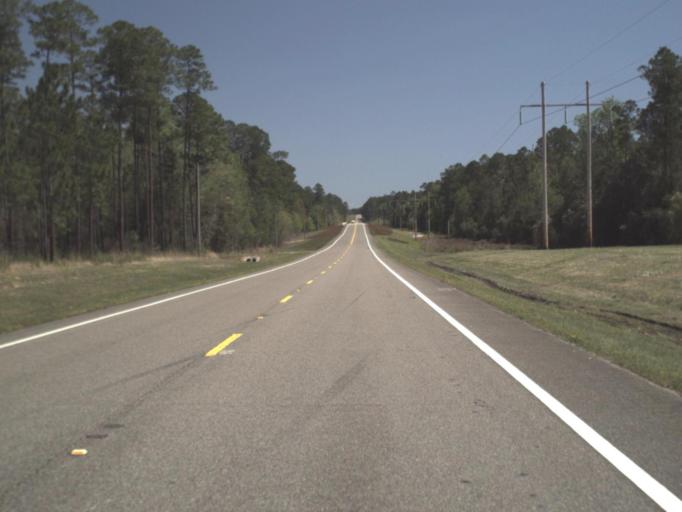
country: US
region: Florida
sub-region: Santa Rosa County
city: Point Baker
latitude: 30.8847
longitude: -86.9636
